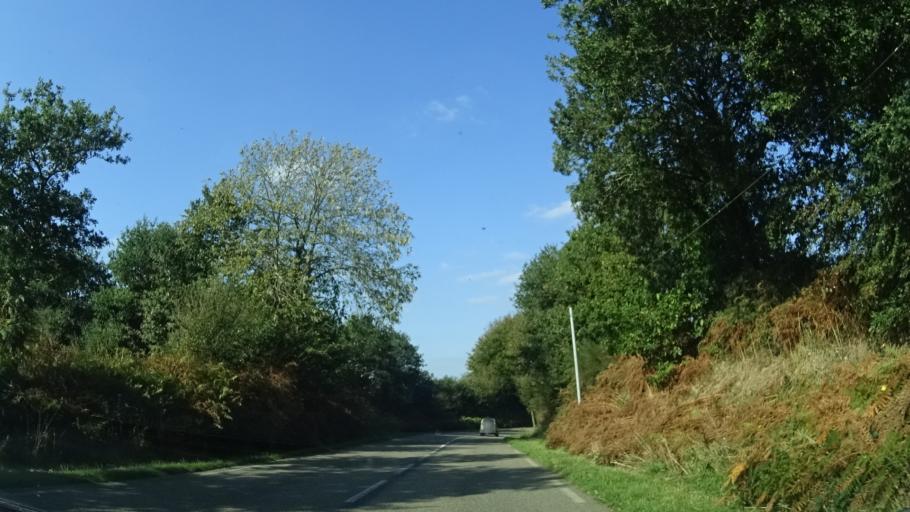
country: FR
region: Brittany
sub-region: Departement du Finistere
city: Cast
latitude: 48.1785
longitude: -4.1134
